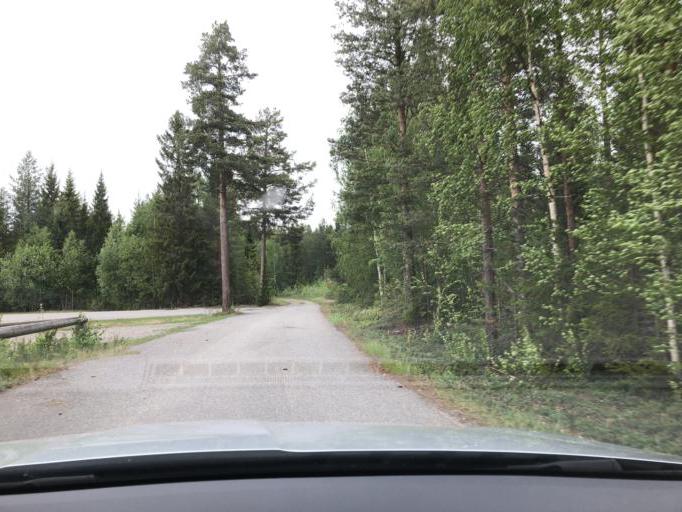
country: SE
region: Norrbotten
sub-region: Pitea Kommun
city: Roknas
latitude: 65.3924
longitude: 21.2692
